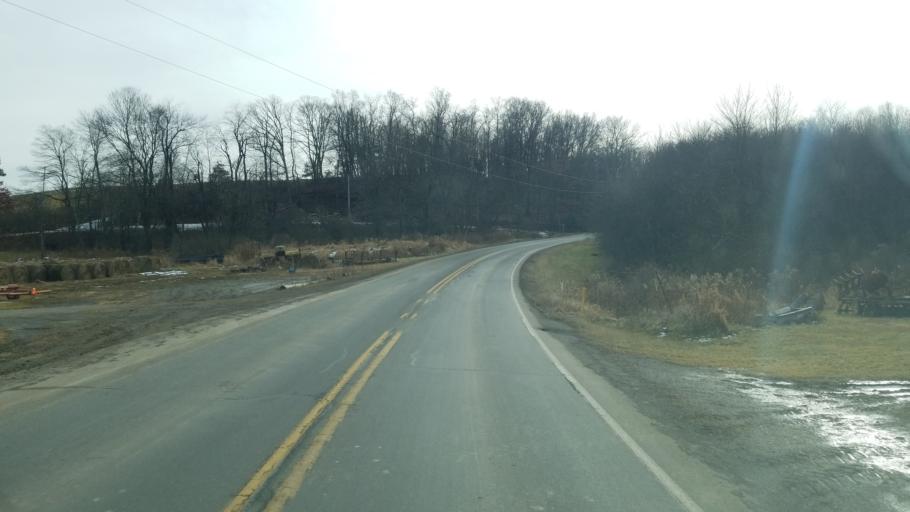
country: US
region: Pennsylvania
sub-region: Jefferson County
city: Punxsutawney
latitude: 40.8899
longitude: -79.0409
